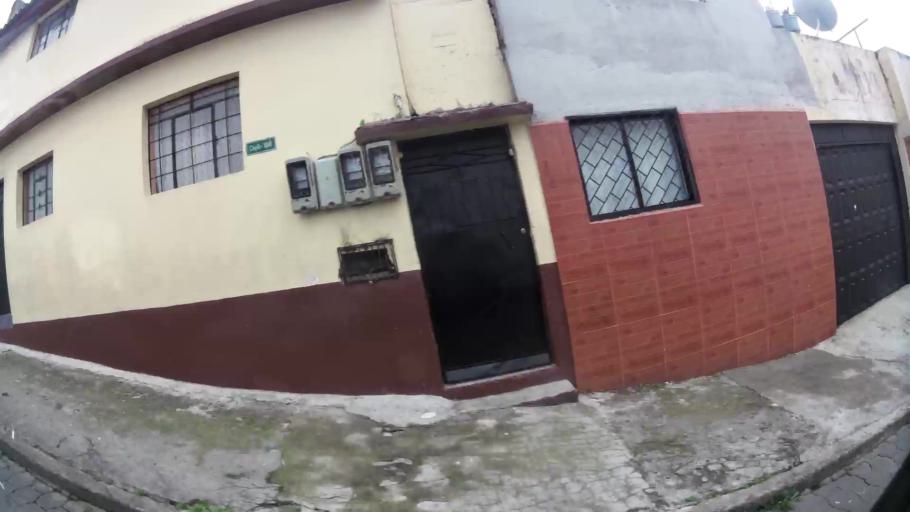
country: EC
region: Pichincha
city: Quito
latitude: -0.2124
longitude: -78.5126
